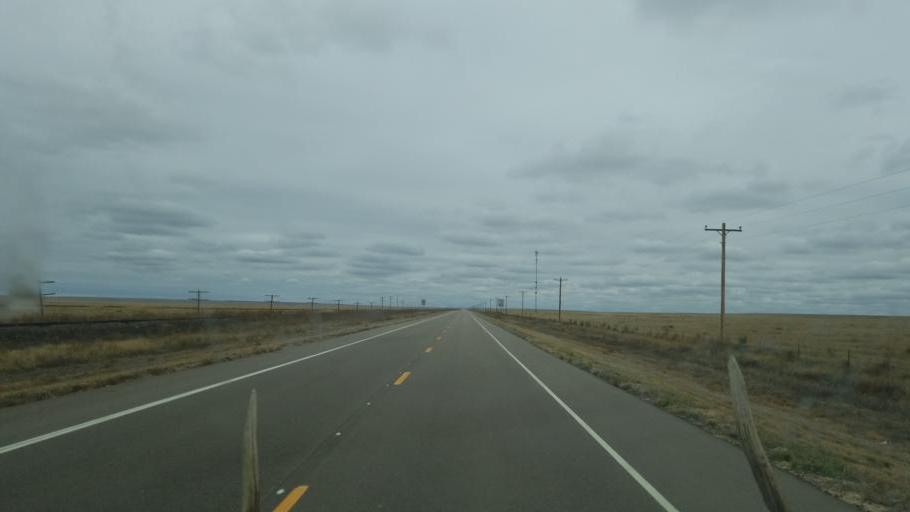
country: US
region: Colorado
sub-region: Bent County
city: Las Animas
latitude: 38.3889
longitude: -103.3101
